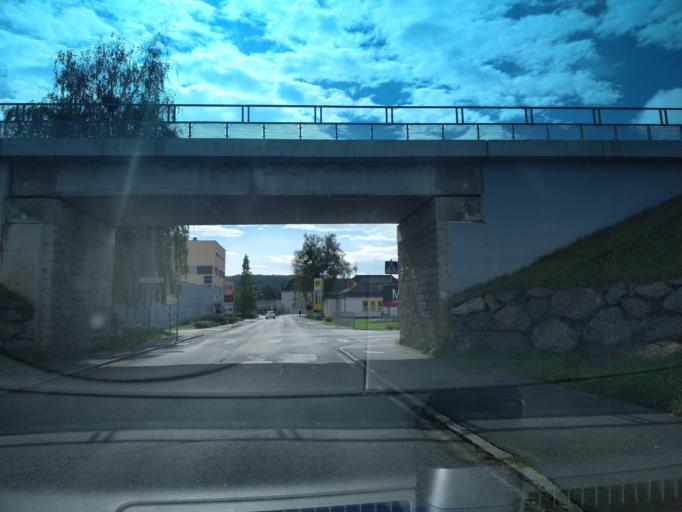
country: AT
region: Styria
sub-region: Politischer Bezirk Deutschlandsberg
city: Deutschlandsberg
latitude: 46.8203
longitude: 15.2253
